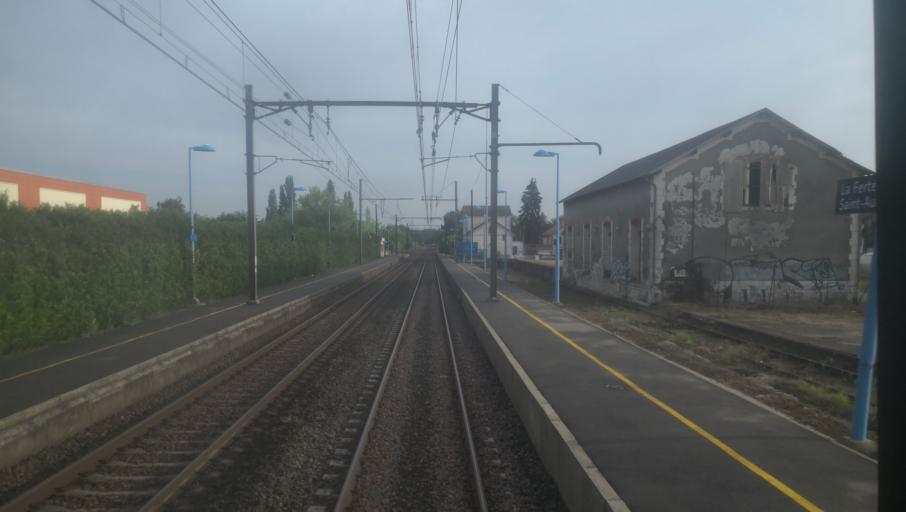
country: FR
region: Centre
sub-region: Departement du Loiret
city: La Ferte-Saint-Aubin
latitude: 47.7197
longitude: 1.9326
